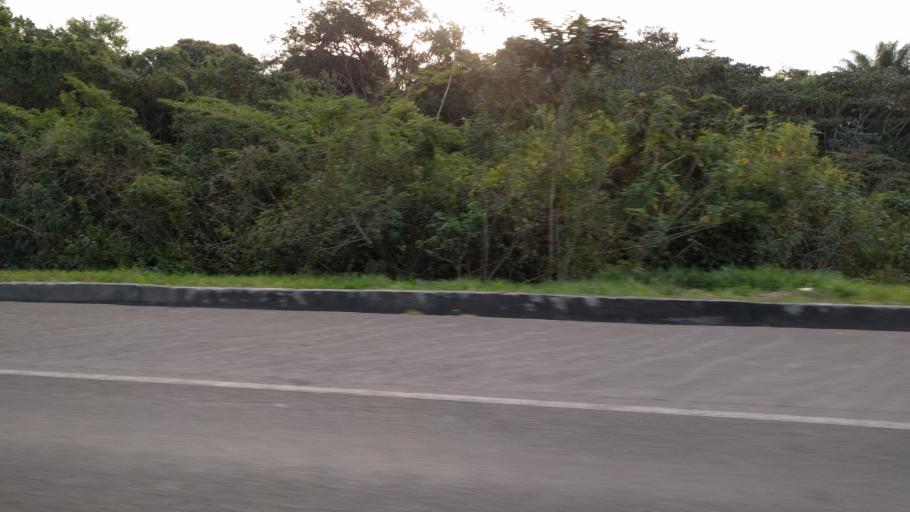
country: BO
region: Santa Cruz
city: Buena Vista
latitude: -17.4167
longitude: -63.6191
